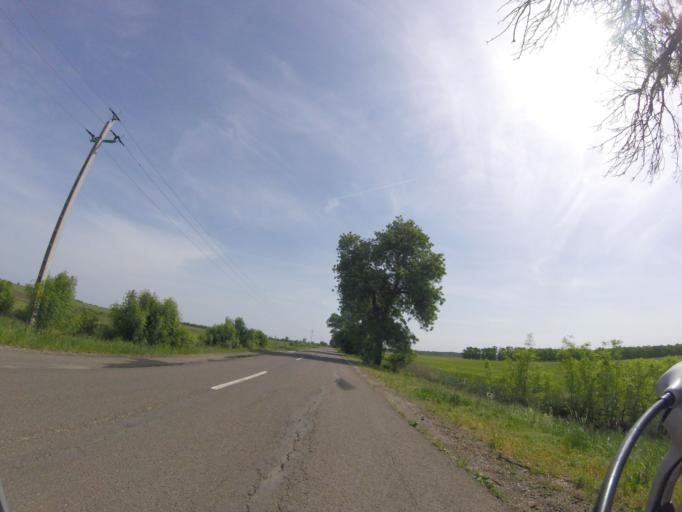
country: HU
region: Jasz-Nagykun-Szolnok
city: Tiszapuspoki
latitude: 47.2631
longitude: 20.3194
